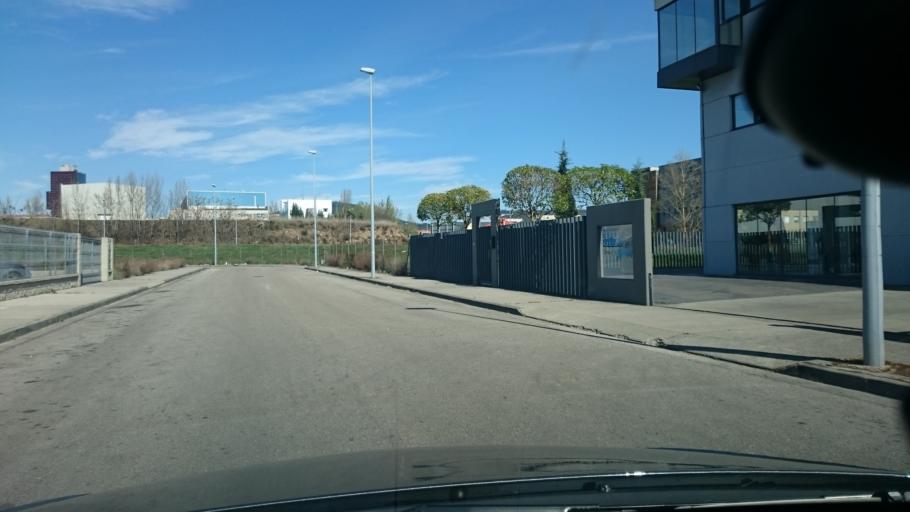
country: ES
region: Castille and Leon
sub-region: Provincia de Leon
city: Ponferrada
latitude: 42.5511
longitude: -6.6143
